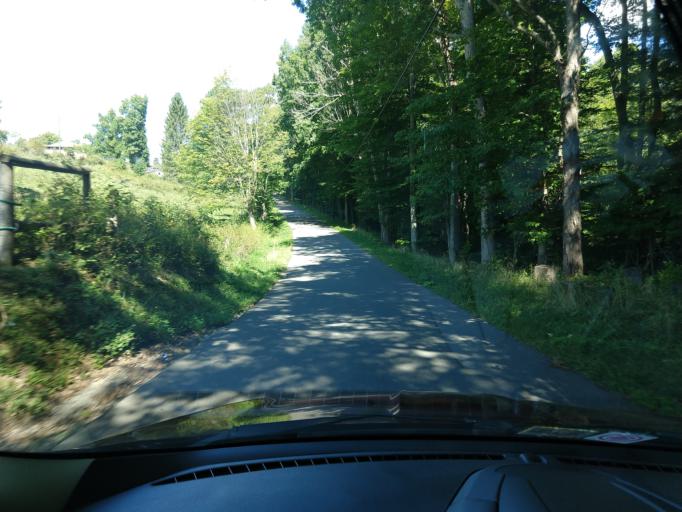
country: US
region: West Virginia
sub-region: Nicholas County
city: Craigsville
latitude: 38.2768
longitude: -80.7167
